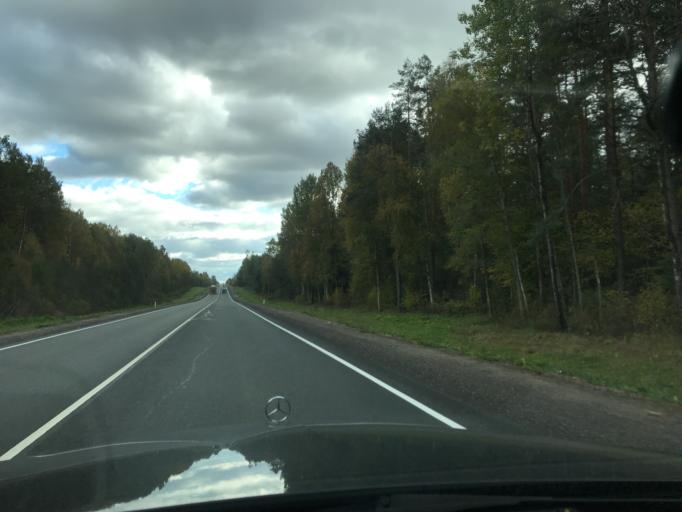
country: RU
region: Pskov
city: Opochka
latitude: 56.9561
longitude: 28.6380
